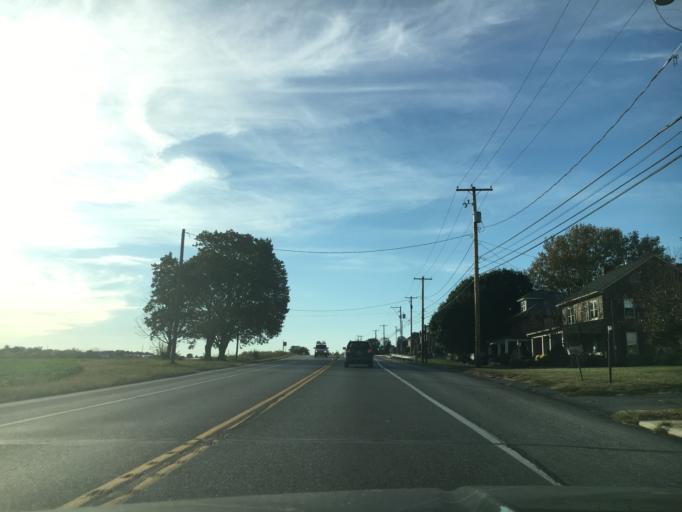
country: US
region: Pennsylvania
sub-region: Lancaster County
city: Ephrata
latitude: 40.1612
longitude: -76.1444
